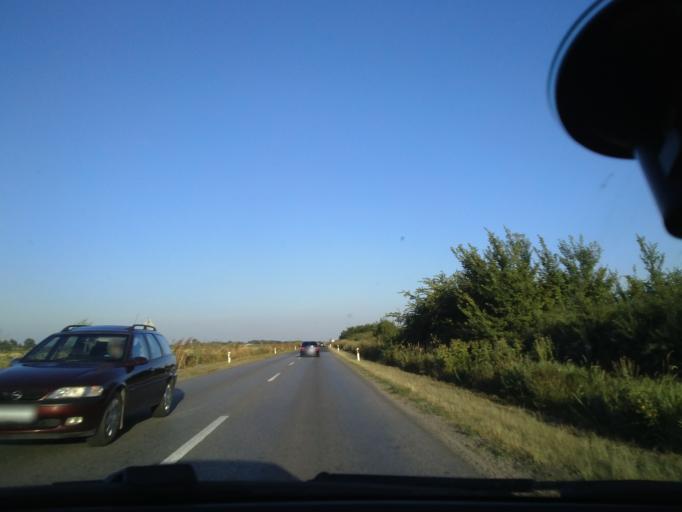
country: RS
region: Autonomna Pokrajina Vojvodina
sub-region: Juznobacki Okrug
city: Backi Petrovac
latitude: 45.3420
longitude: 19.6469
